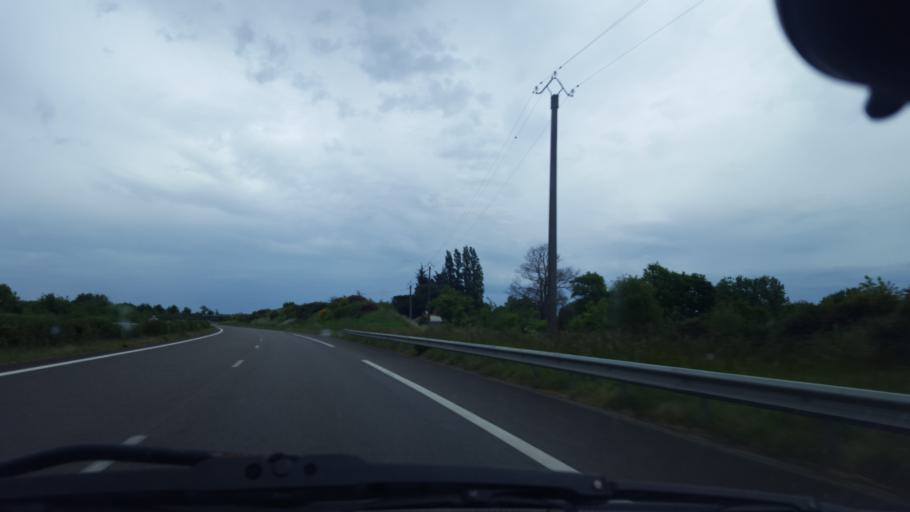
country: FR
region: Pays de la Loire
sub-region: Departement de la Loire-Atlantique
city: Saint-Philbert-de-Grand-Lieu
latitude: 47.0534
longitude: -1.6257
